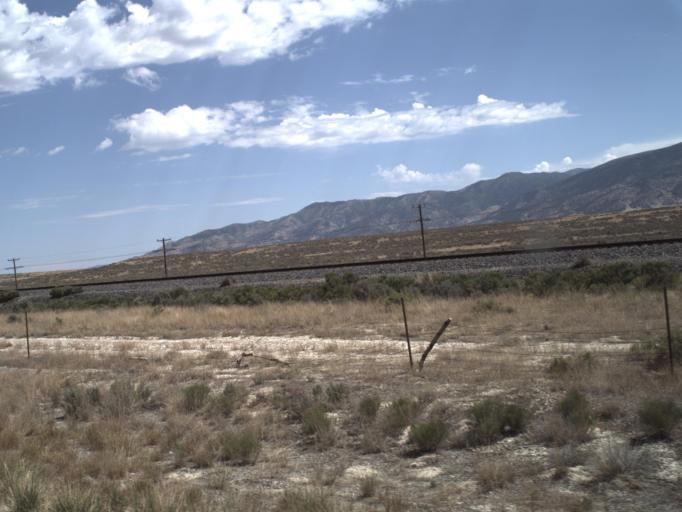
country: US
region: Utah
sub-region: Tooele County
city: Tooele
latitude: 40.3409
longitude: -112.4103
